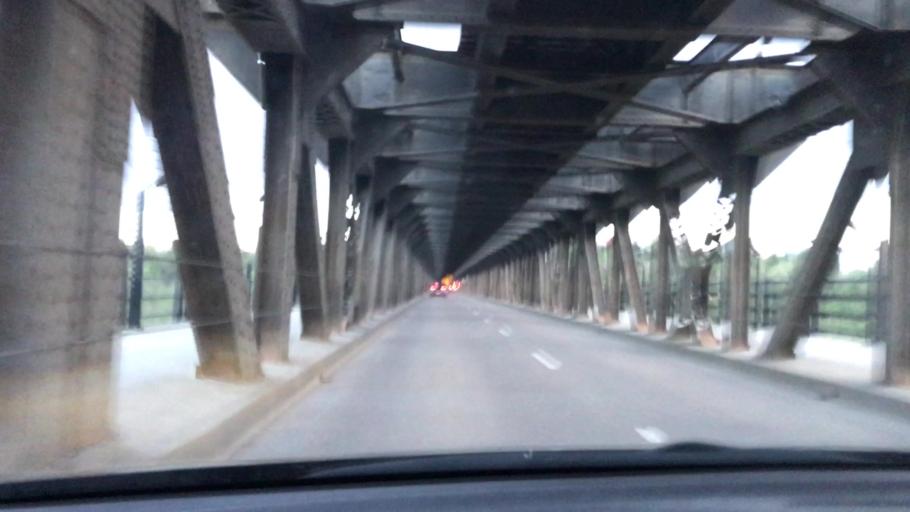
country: CA
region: Alberta
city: Edmonton
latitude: 53.5290
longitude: -113.5116
